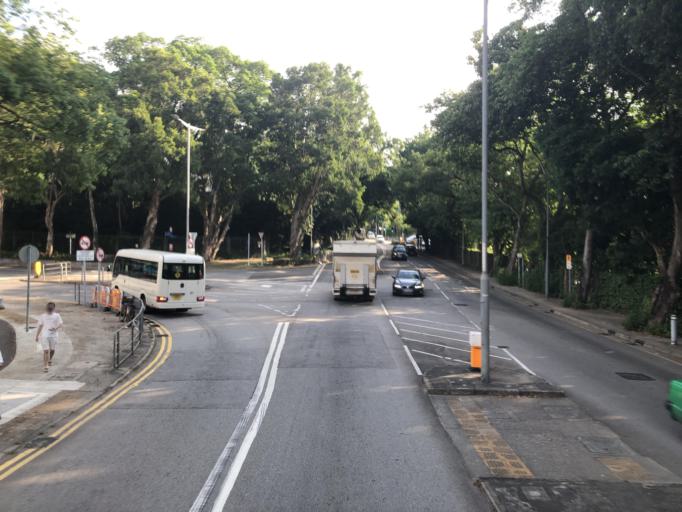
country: HK
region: Tai Po
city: Tai Po
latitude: 22.4972
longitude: 114.1226
